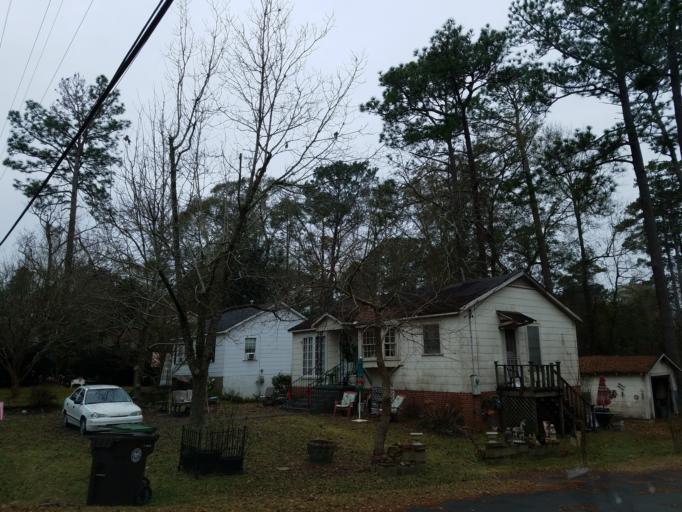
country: US
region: Mississippi
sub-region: Forrest County
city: Hattiesburg
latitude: 31.3184
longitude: -89.3185
